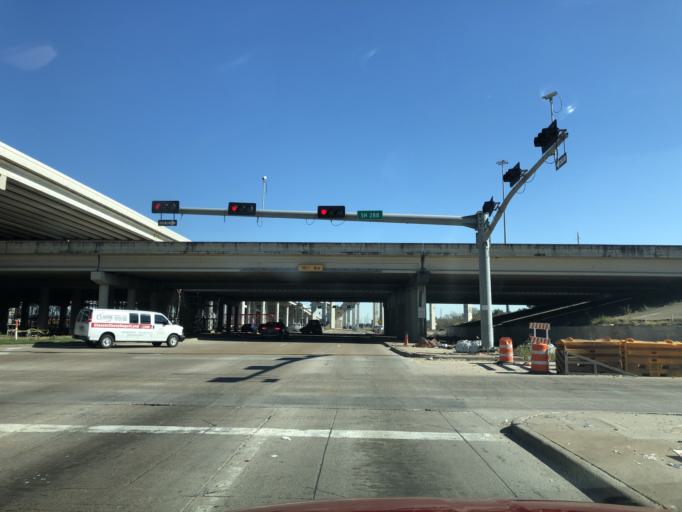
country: US
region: Texas
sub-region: Brazoria County
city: Brookside Village
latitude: 29.5968
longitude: -95.3874
